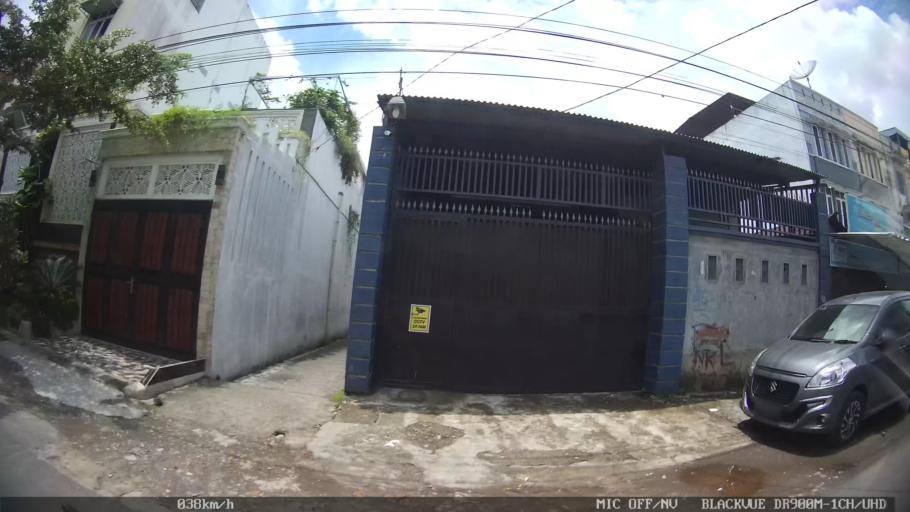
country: ID
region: North Sumatra
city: Medan
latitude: 3.5946
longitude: 98.7089
